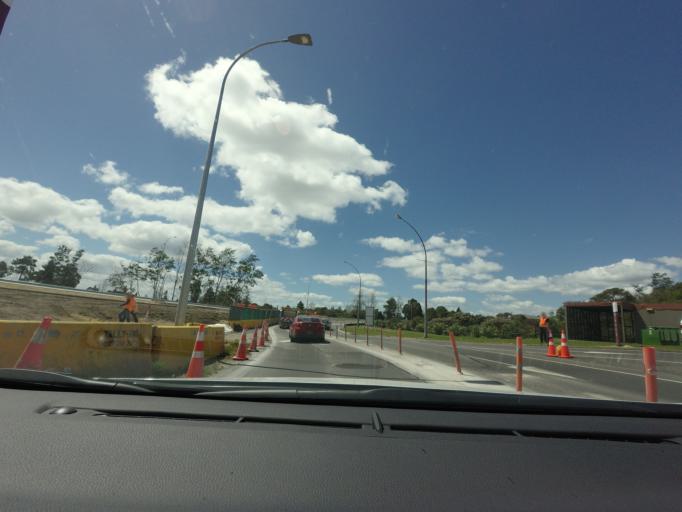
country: NZ
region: Bay of Plenty
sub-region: Rotorua District
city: Rotorua
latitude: -38.1649
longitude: 176.2474
